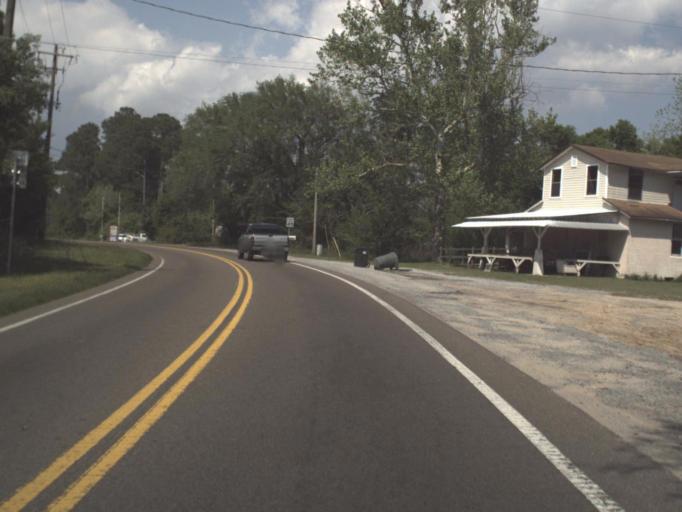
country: US
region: Florida
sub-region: Escambia County
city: Myrtle Grove
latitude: 30.4038
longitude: -87.3735
